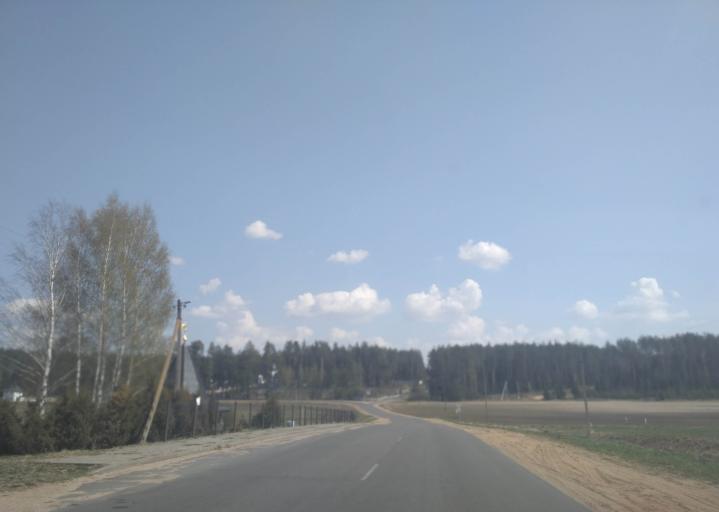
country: BY
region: Minsk
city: Loshnitsa
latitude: 54.4923
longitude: 28.6758
